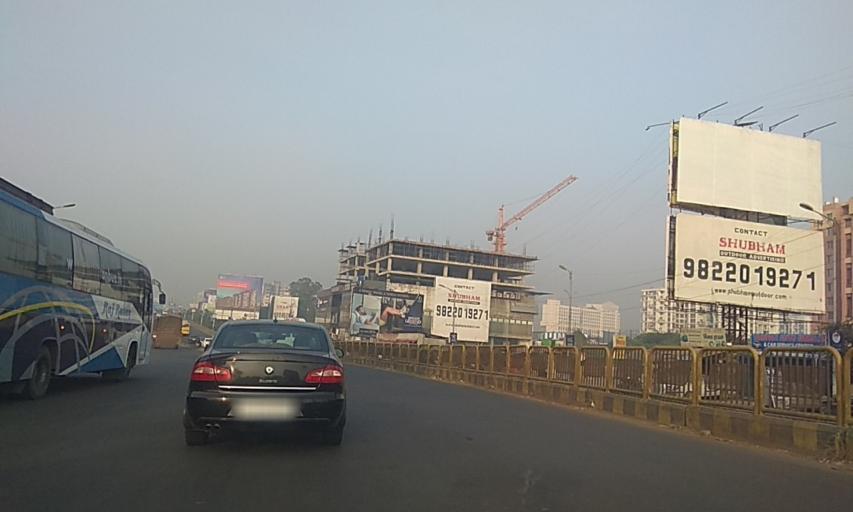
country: IN
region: Maharashtra
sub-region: Pune Division
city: Pimpri
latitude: 18.5924
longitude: 73.7613
